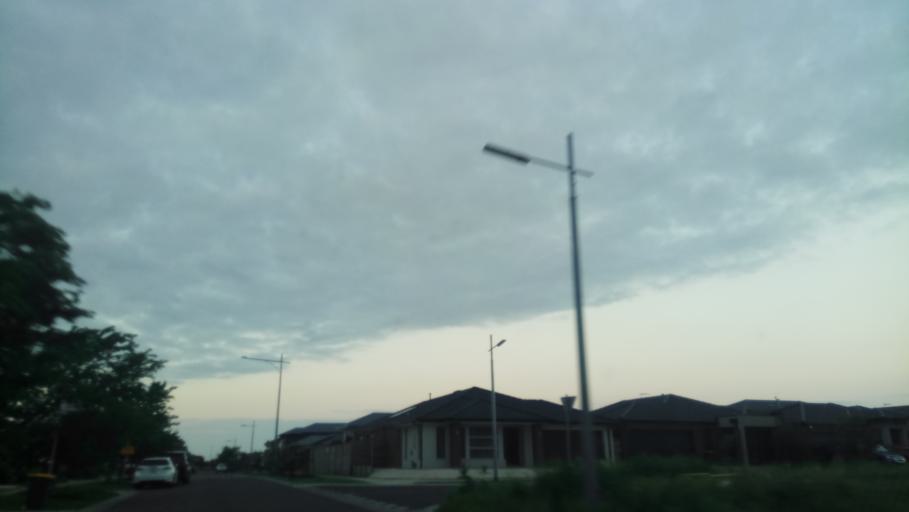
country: AU
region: Victoria
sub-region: Wyndham
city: Point Cook
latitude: -37.9138
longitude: 144.7581
